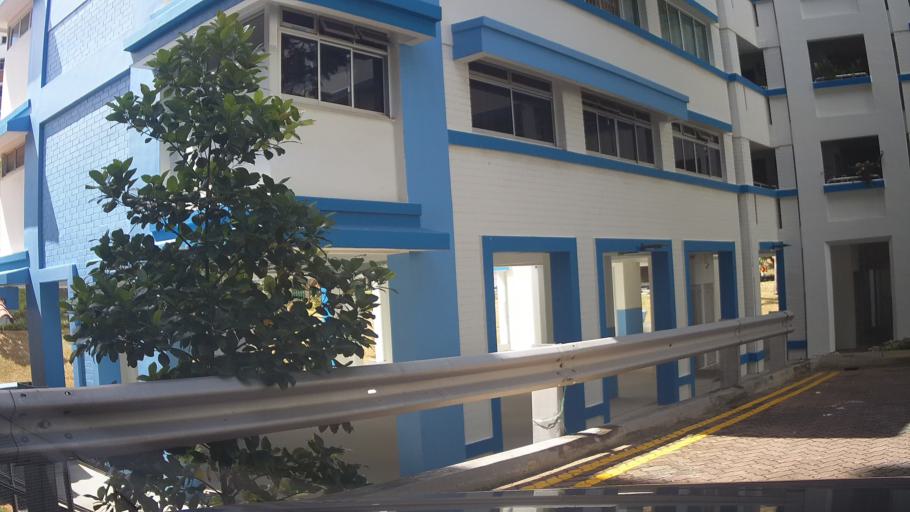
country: SG
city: Singapore
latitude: 1.3645
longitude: 103.9608
